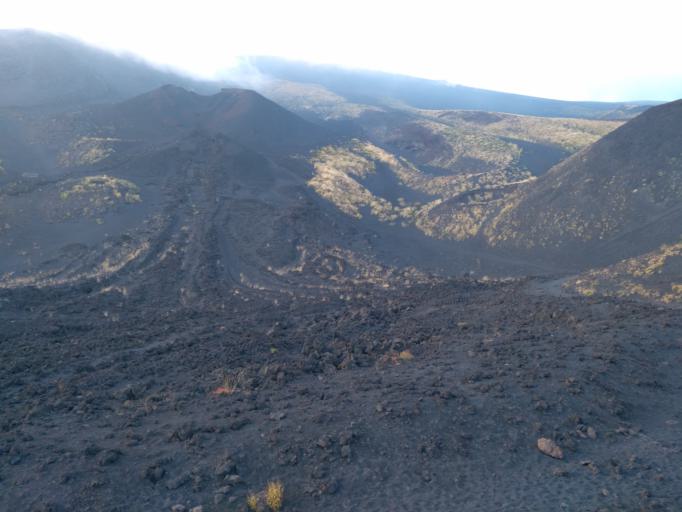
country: IT
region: Sicily
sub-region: Catania
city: Nicolosi
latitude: 37.7040
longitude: 15.0063
